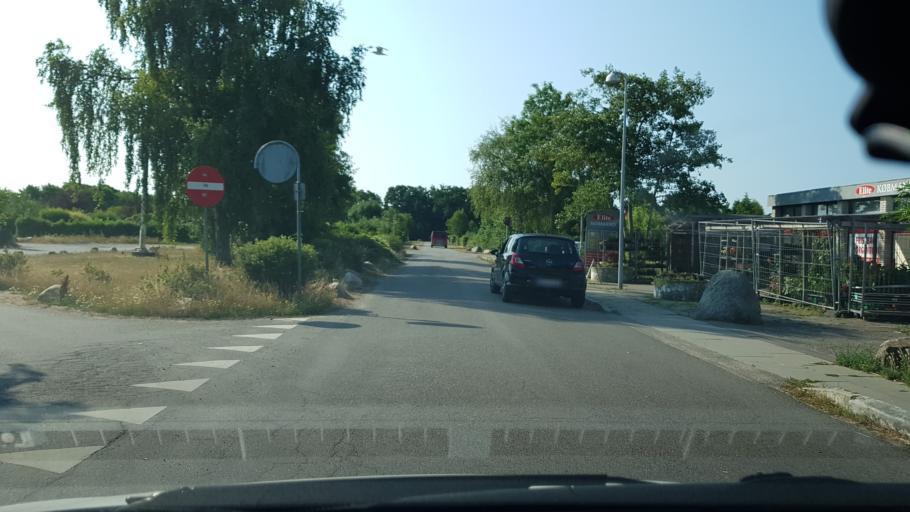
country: DK
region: Capital Region
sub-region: Brondby Kommune
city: Brondbyvester
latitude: 55.6342
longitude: 12.3945
